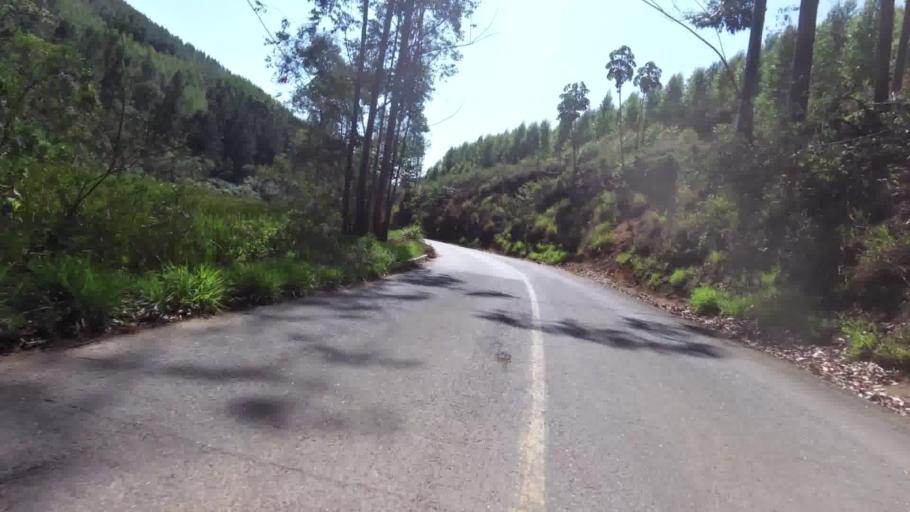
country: BR
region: Espirito Santo
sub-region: Marechal Floriano
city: Marechal Floriano
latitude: -20.4414
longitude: -40.8829
